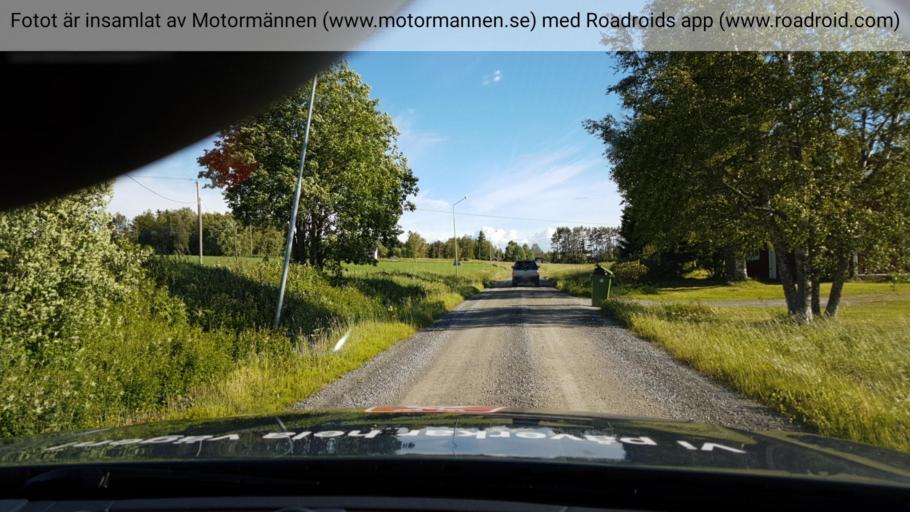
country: SE
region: Jaemtland
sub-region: Bergs Kommun
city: Hoverberg
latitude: 63.0255
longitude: 14.3731
